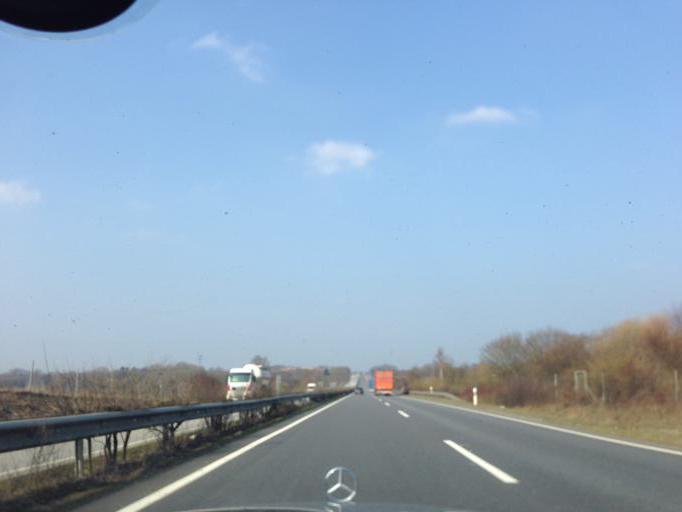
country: DE
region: Schleswig-Holstein
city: Hogersdorf
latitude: 53.9077
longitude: 10.2752
